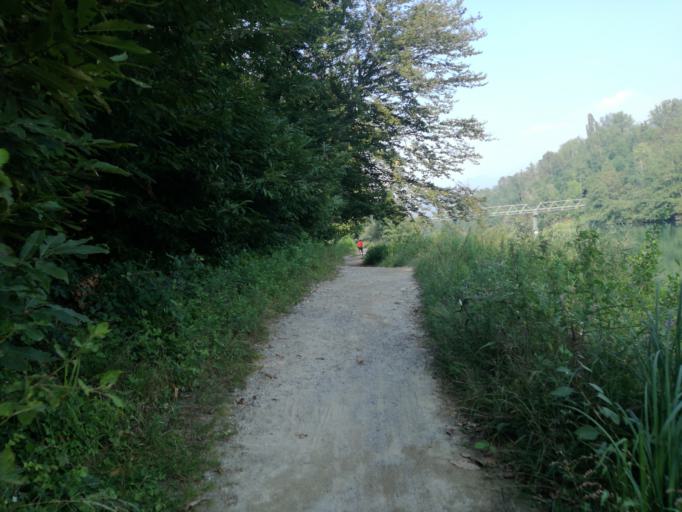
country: IT
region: Lombardy
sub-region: Provincia di Lecco
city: Imbersago
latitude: 45.7145
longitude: 9.4487
